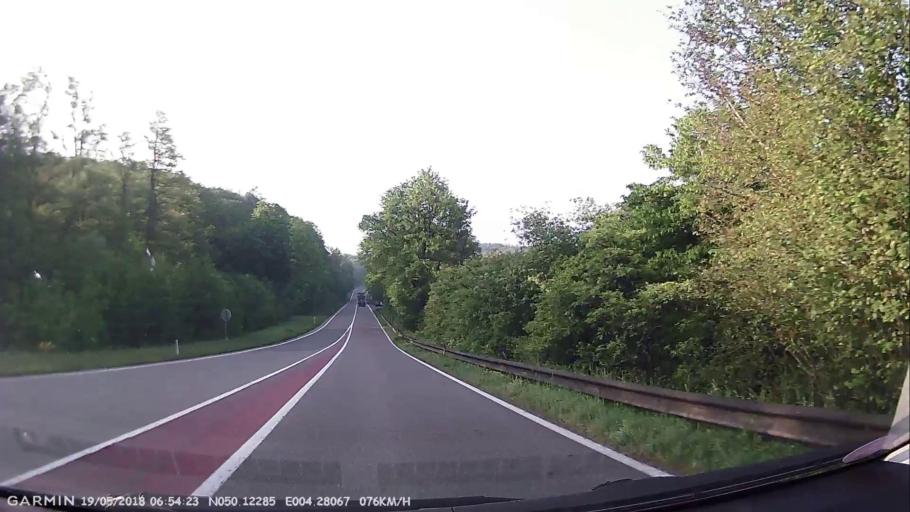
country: BE
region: Wallonia
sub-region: Province du Hainaut
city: Froidchapelle
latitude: 50.1226
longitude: 4.2808
